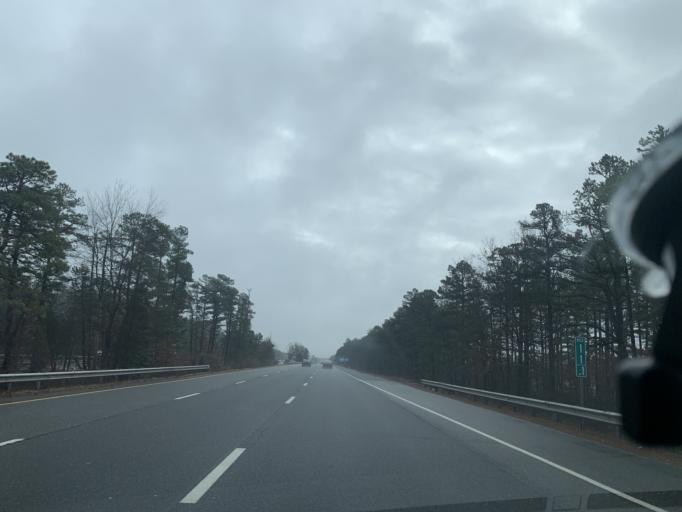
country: US
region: New Jersey
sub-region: Atlantic County
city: Pomona
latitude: 39.4438
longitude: -74.6137
